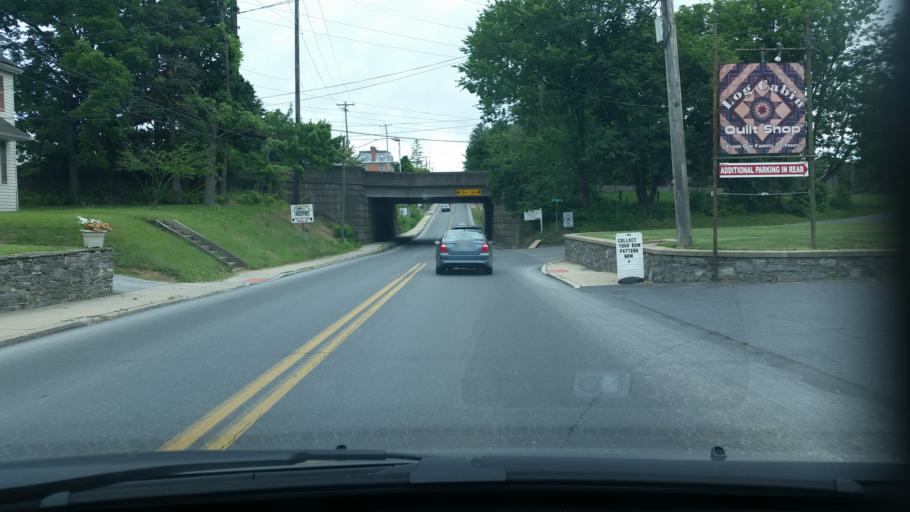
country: US
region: Pennsylvania
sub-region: Lancaster County
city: Strasburg
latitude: 40.0387
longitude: -76.1811
